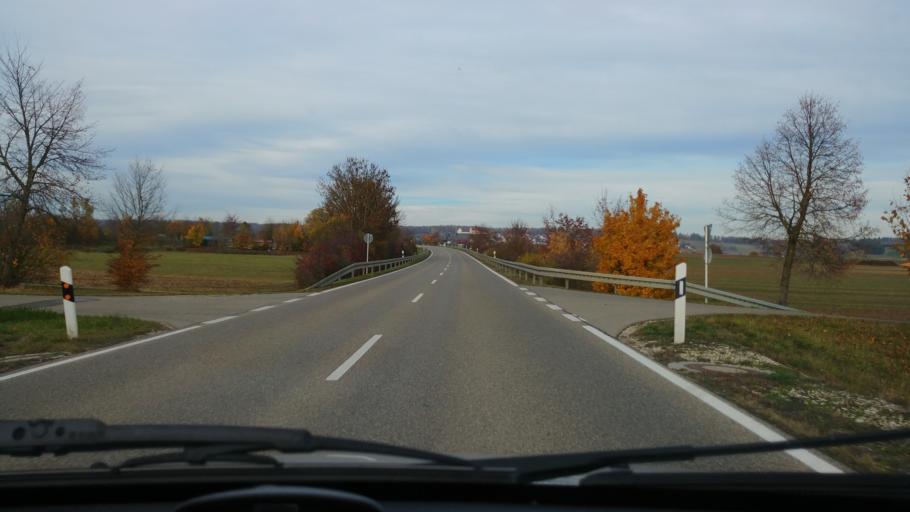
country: DE
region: Bavaria
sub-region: Swabia
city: Bachhagel
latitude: 48.6413
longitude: 10.2958
